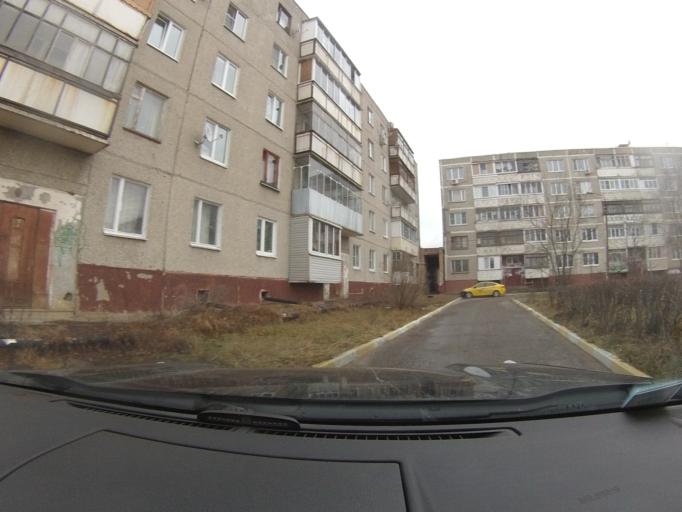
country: RU
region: Moskovskaya
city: Lopatinskiy
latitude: 55.3376
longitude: 38.7130
